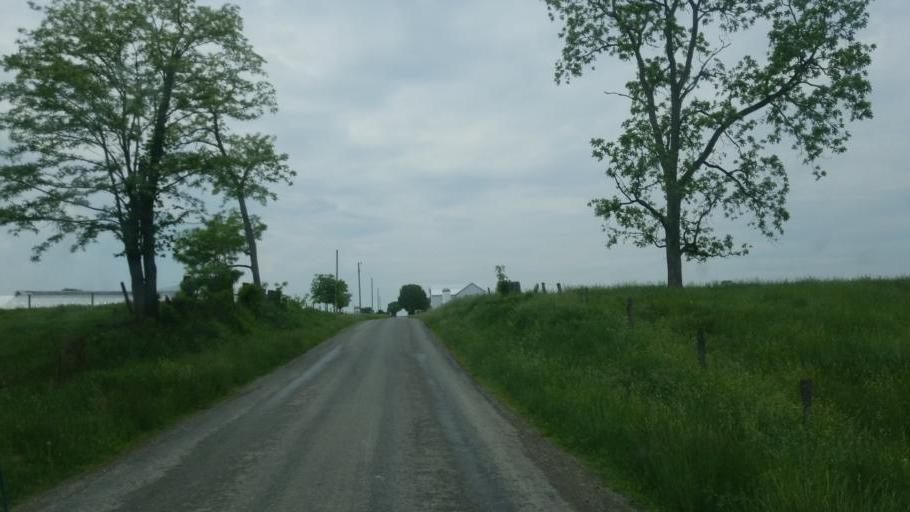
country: US
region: Ohio
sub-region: Wayne County
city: Apple Creek
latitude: 40.7780
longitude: -81.7801
